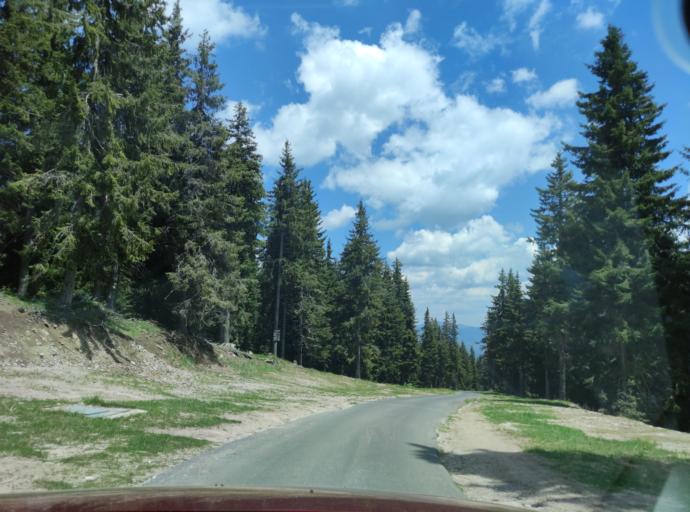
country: BG
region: Smolyan
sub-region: Obshtina Smolyan
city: Smolyan
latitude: 41.6367
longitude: 24.6826
